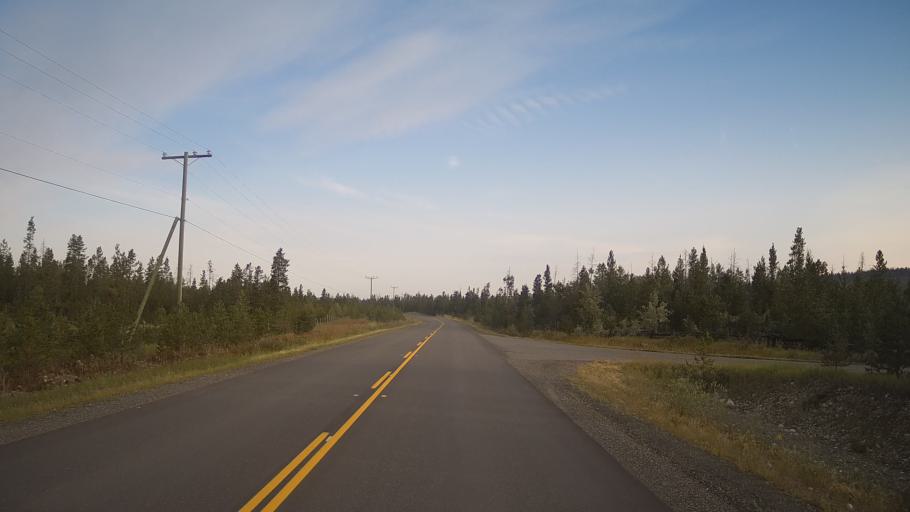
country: CA
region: British Columbia
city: Hanceville
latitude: 52.1347
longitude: -123.7008
